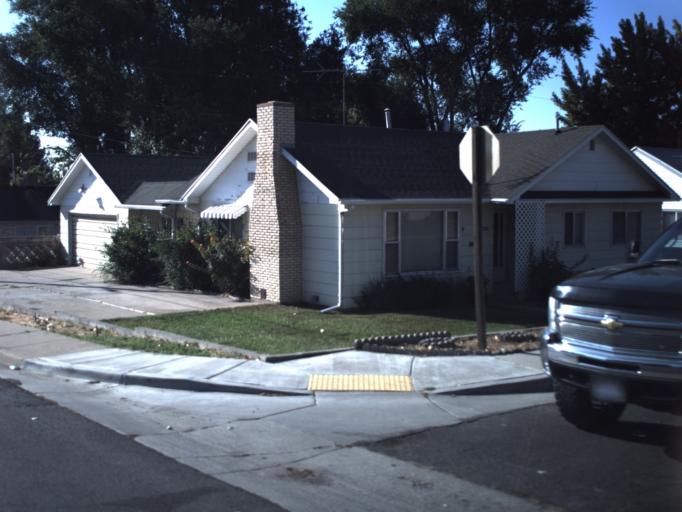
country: US
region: Utah
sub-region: Davis County
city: Sunset
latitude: 41.1399
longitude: -112.0299
